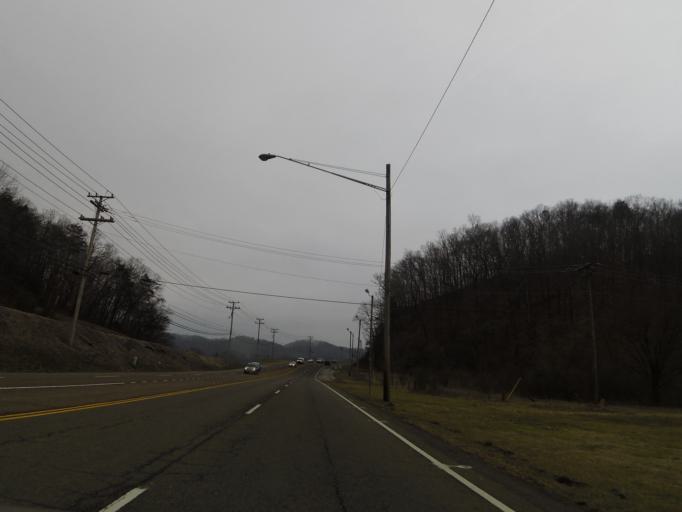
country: US
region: Tennessee
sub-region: Anderson County
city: Clinton
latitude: 36.0907
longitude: -84.1293
